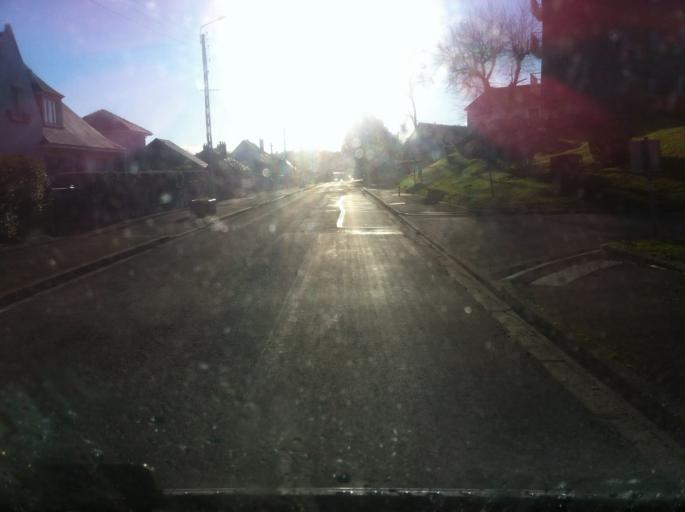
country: FR
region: Haute-Normandie
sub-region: Departement de la Seine-Maritime
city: Le Treport
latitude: 50.0573
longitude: 1.3682
